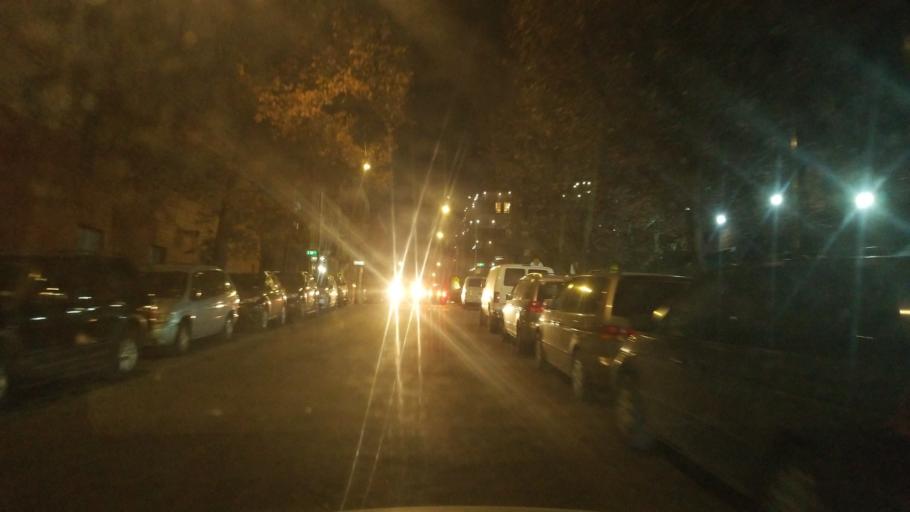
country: US
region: New York
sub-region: New York County
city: Manhattan
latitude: 40.8077
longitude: -73.9201
